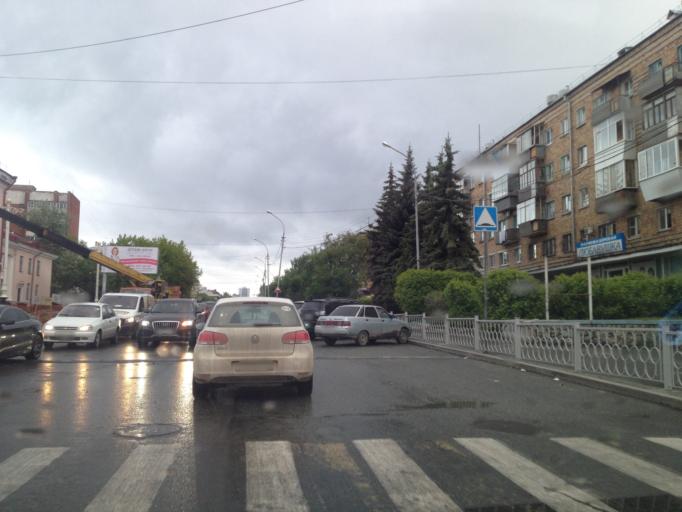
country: RU
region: Sverdlovsk
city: Yekaterinburg
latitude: 56.8391
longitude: 60.5538
